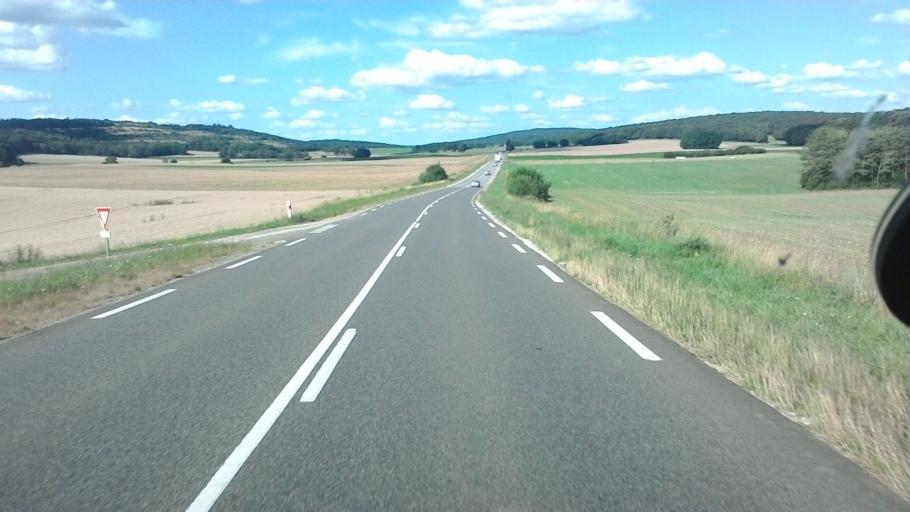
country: FR
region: Franche-Comte
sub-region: Departement de la Haute-Saone
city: Noidans-les-Vesoul
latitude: 47.5589
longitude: 6.0685
